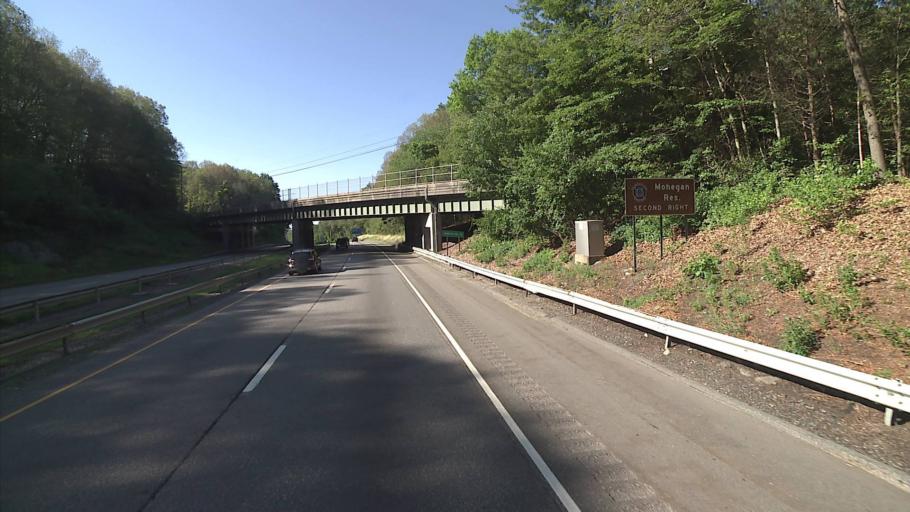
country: US
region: Connecticut
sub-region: New London County
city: Norwich
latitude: 41.5182
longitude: -72.1197
